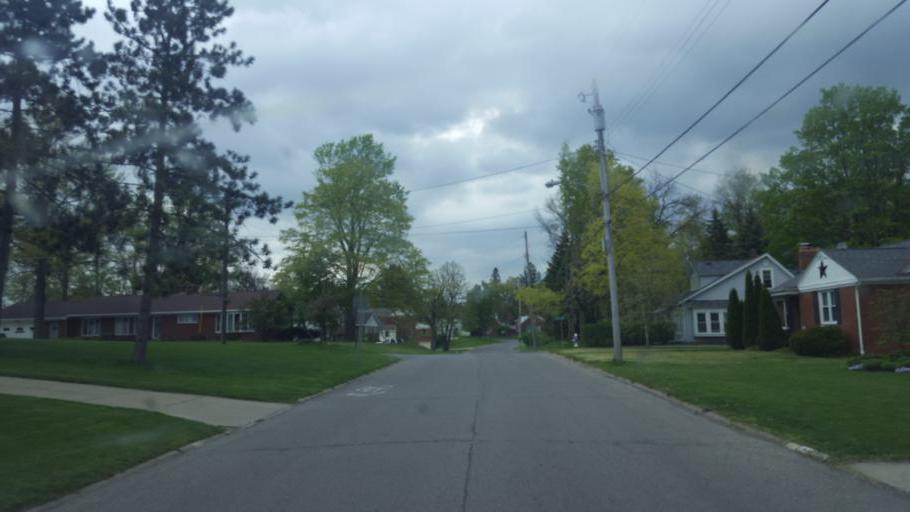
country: US
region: Ohio
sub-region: Richland County
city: Mansfield
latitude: 40.7516
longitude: -82.5481
